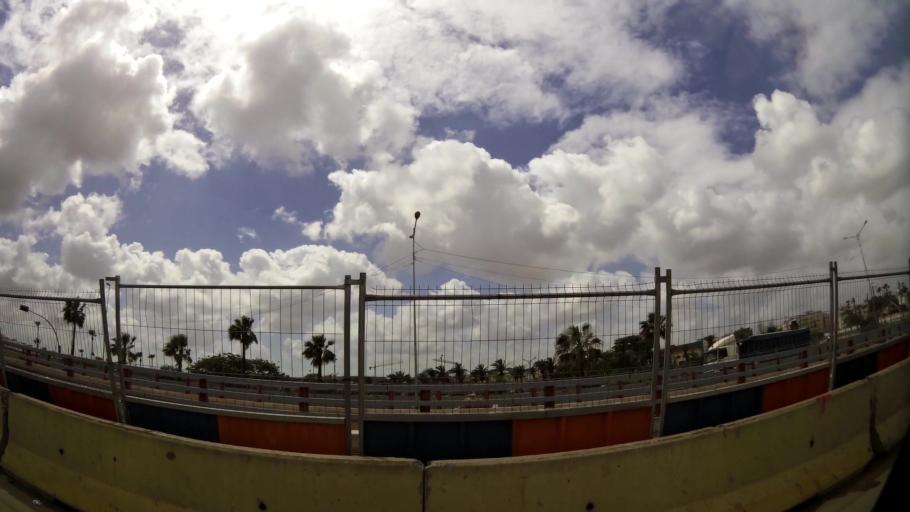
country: MA
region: Grand Casablanca
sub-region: Mediouna
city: Tit Mellil
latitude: 33.6035
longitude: -7.5294
